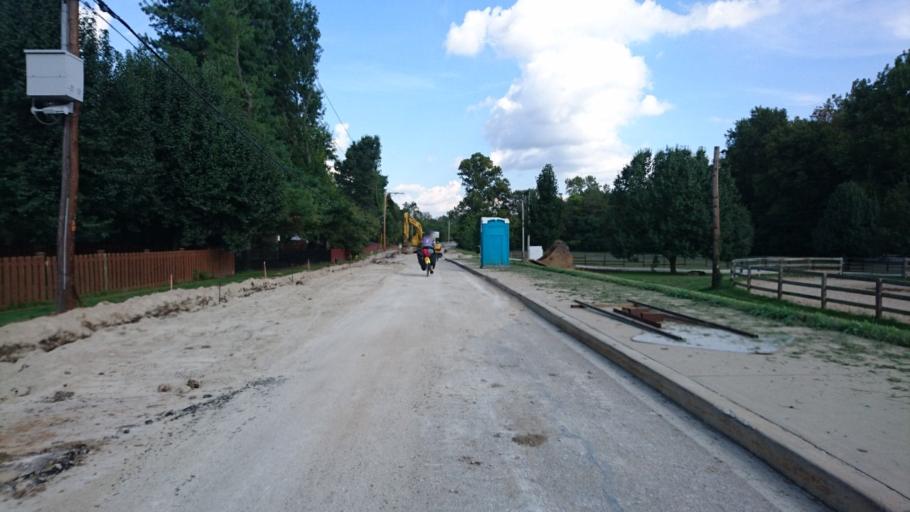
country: US
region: Missouri
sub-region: Saint Louis County
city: Eureka
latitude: 38.5168
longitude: -90.6408
